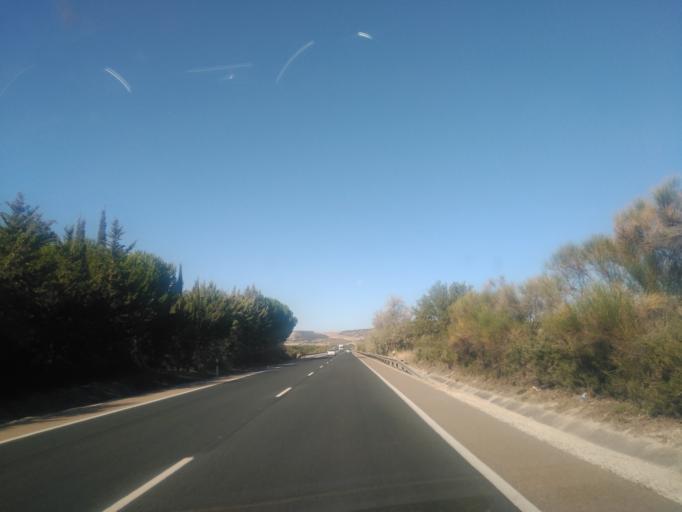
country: ES
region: Castille and Leon
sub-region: Provincia de Valladolid
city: Quintanilla de Onesimo
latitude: 41.6199
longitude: -4.3703
